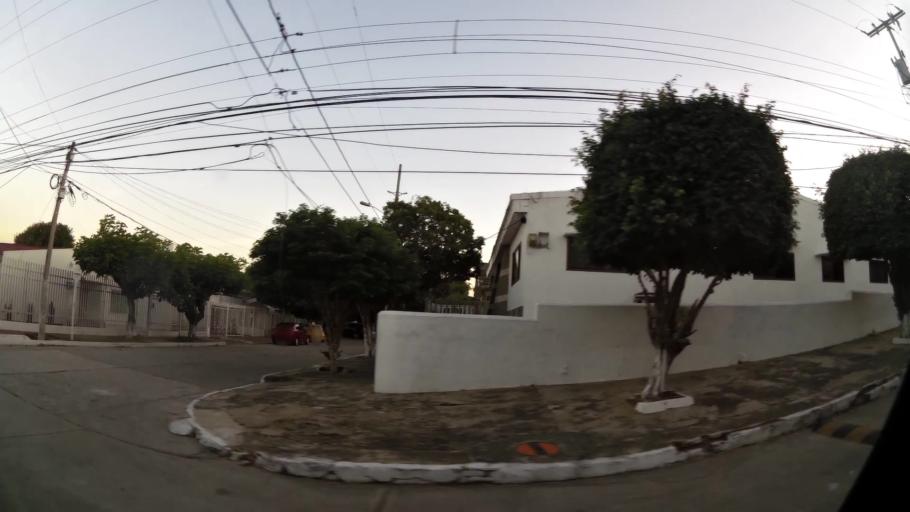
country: CO
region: Atlantico
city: Barranquilla
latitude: 10.9787
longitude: -74.8112
